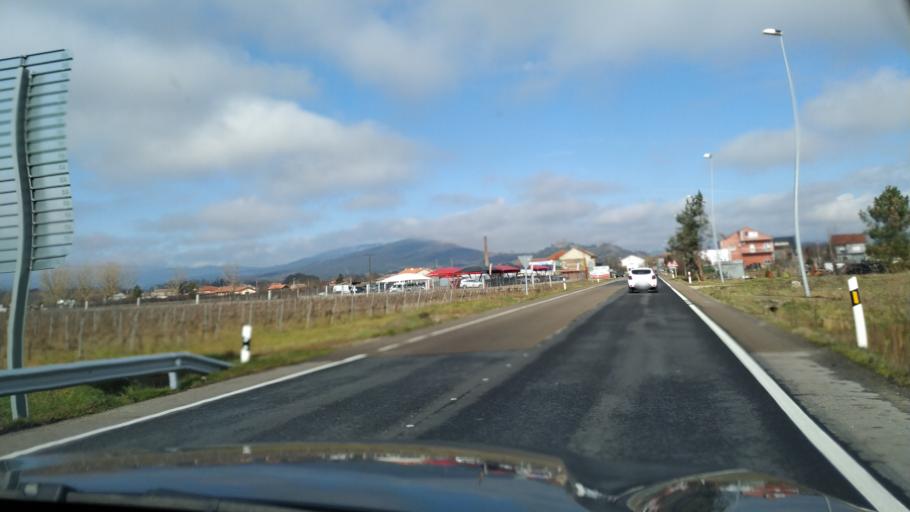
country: ES
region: Galicia
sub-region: Provincia de Ourense
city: Verin
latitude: 41.9145
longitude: -7.4432
